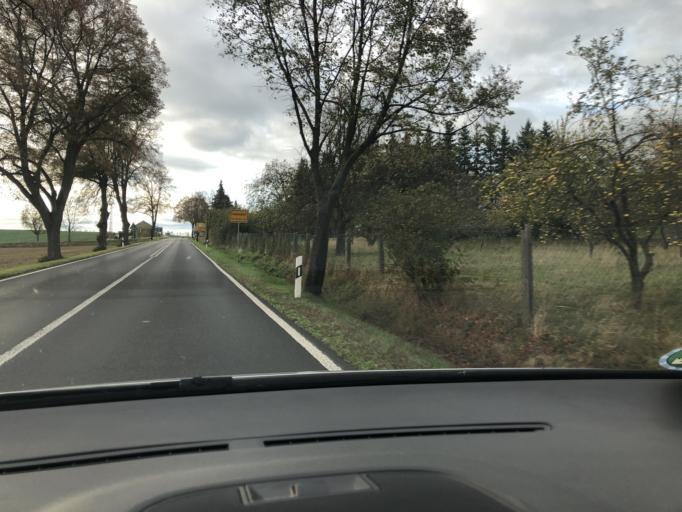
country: DE
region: Thuringia
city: Frankendorf
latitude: 50.9667
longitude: 11.4530
